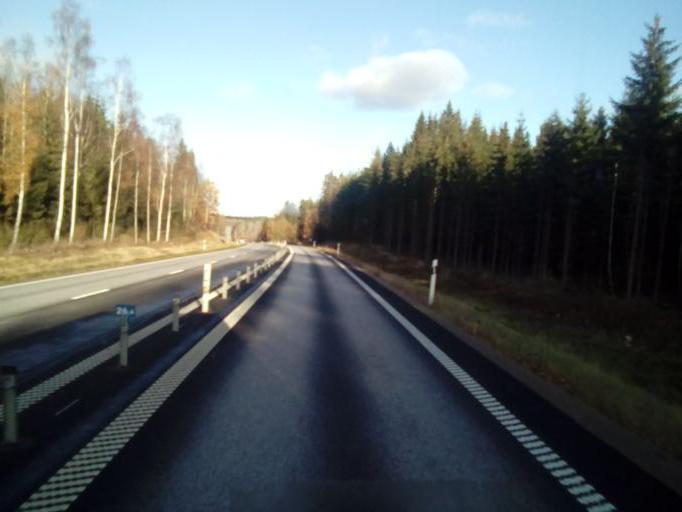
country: SE
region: Kalmar
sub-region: Vimmerby Kommun
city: Vimmerby
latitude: 57.6841
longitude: 15.9931
